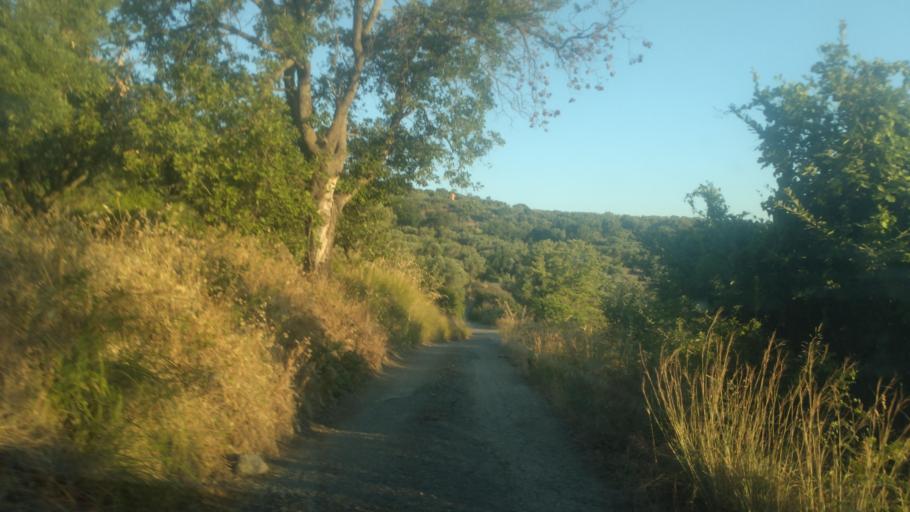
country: IT
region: Calabria
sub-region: Provincia di Catanzaro
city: Staletti
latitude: 38.7726
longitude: 16.5500
